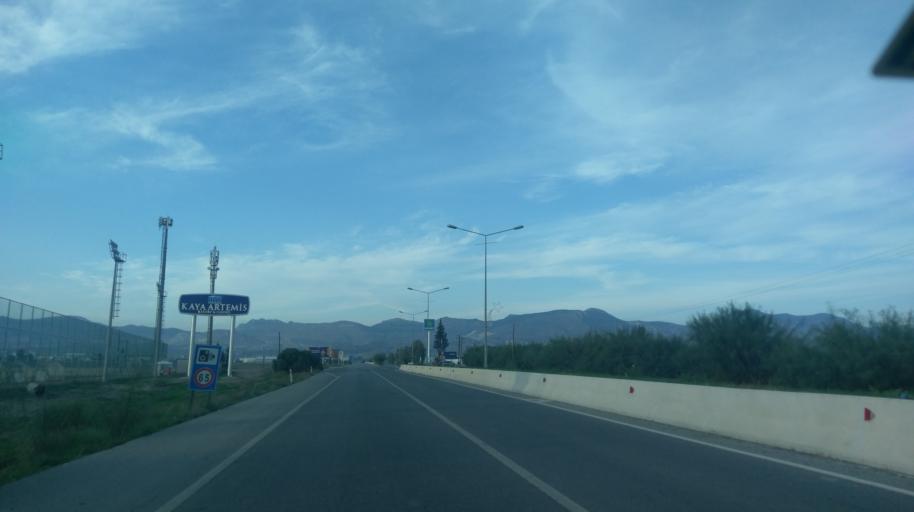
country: CY
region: Lefkosia
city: Geri
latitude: 35.2070
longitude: 33.4989
